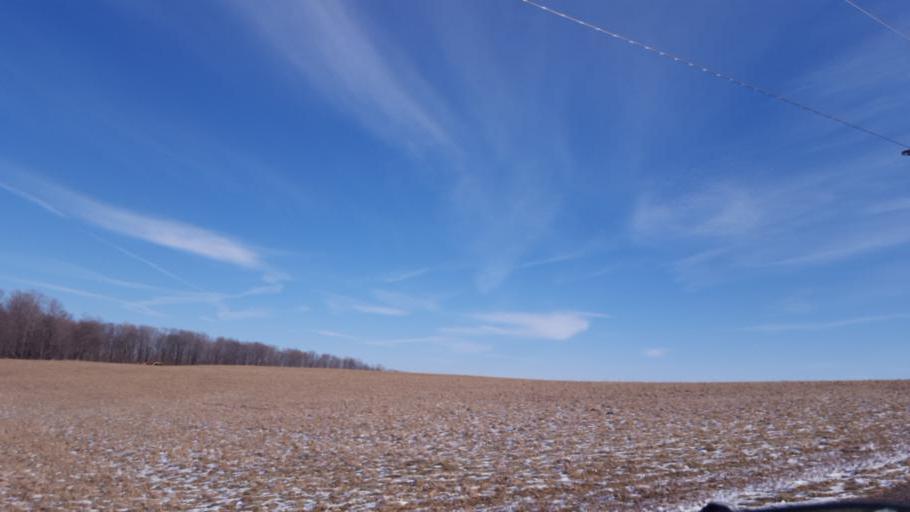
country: US
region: New York
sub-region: Allegany County
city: Wellsville
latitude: 42.1014
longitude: -77.9955
